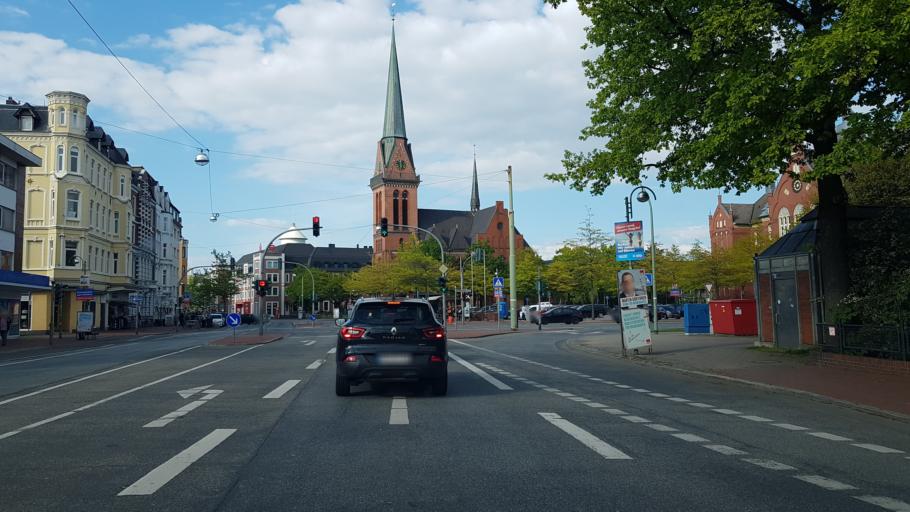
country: DE
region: Bremen
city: Bremerhaven
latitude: 53.5571
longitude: 8.5848
